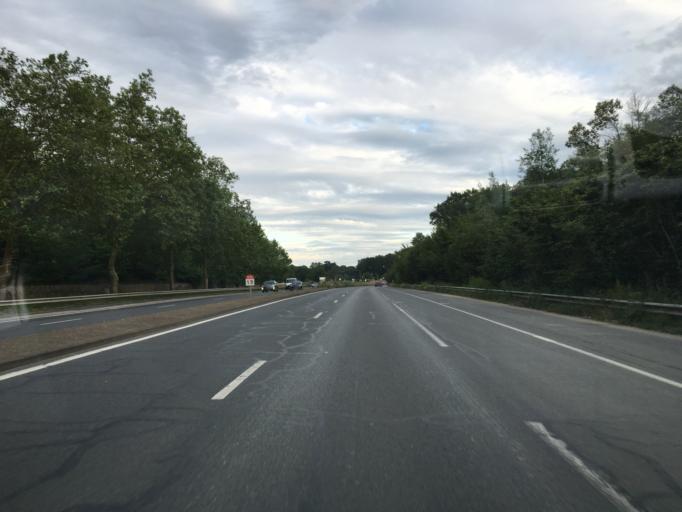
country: FR
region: Ile-de-France
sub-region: Departement du Val-de-Marne
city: Boissy-Saint-Leger
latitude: 48.7379
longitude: 2.5173
